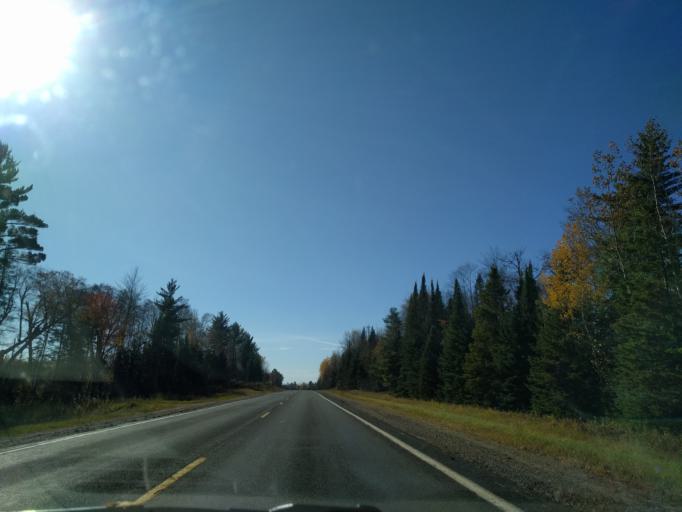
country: US
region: Michigan
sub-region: Marquette County
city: West Ishpeming
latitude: 46.3035
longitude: -87.9913
